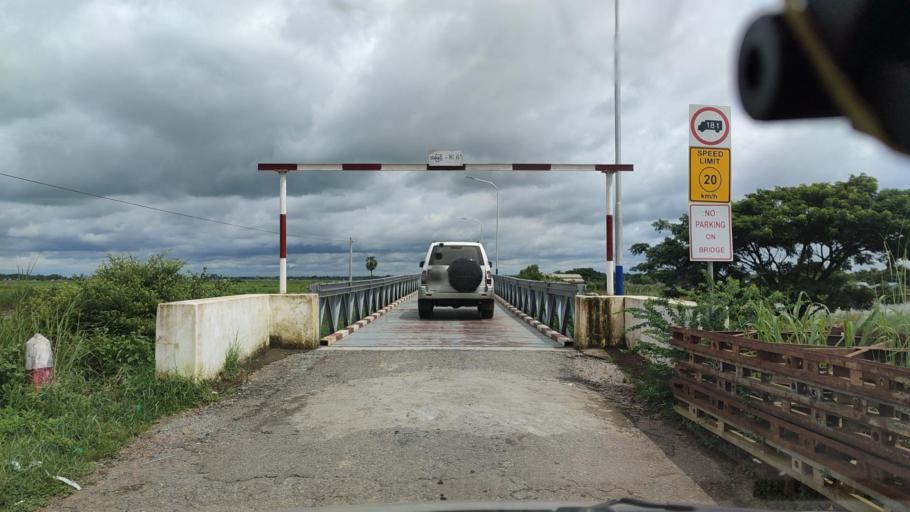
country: MM
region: Bago
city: Thanatpin
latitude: 17.0938
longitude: 96.4502
